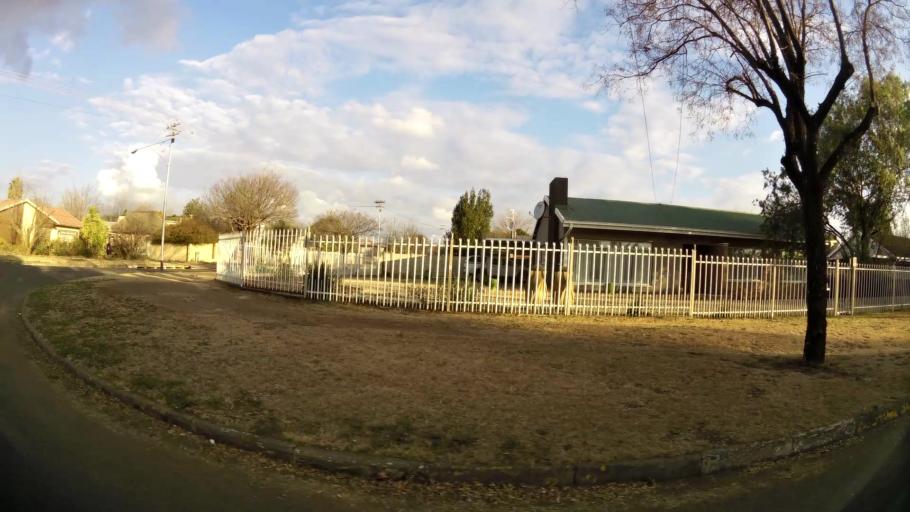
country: ZA
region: Orange Free State
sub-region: Mangaung Metropolitan Municipality
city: Bloemfontein
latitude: -29.1430
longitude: 26.1920
